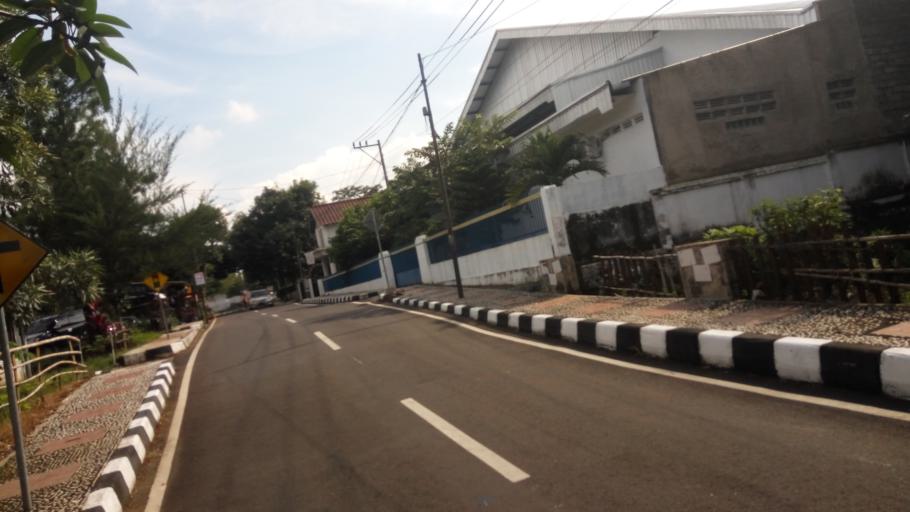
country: ID
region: Central Java
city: Ungaran
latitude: -7.1351
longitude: 110.4126
